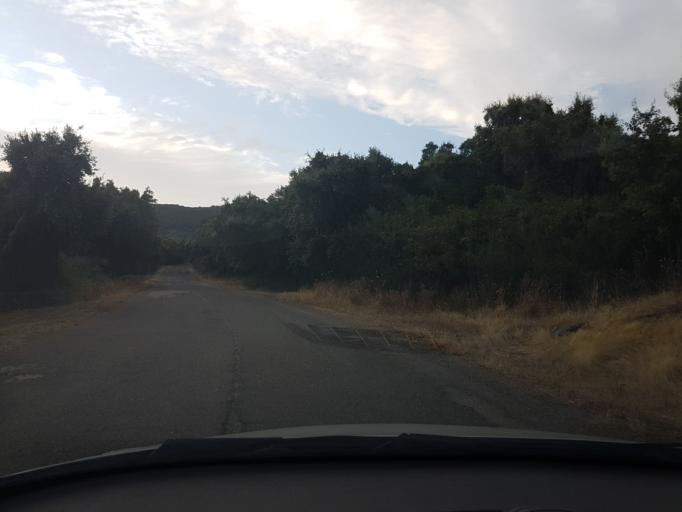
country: IT
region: Sardinia
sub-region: Provincia di Oristano
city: Seneghe
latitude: 40.1079
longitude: 8.6226
